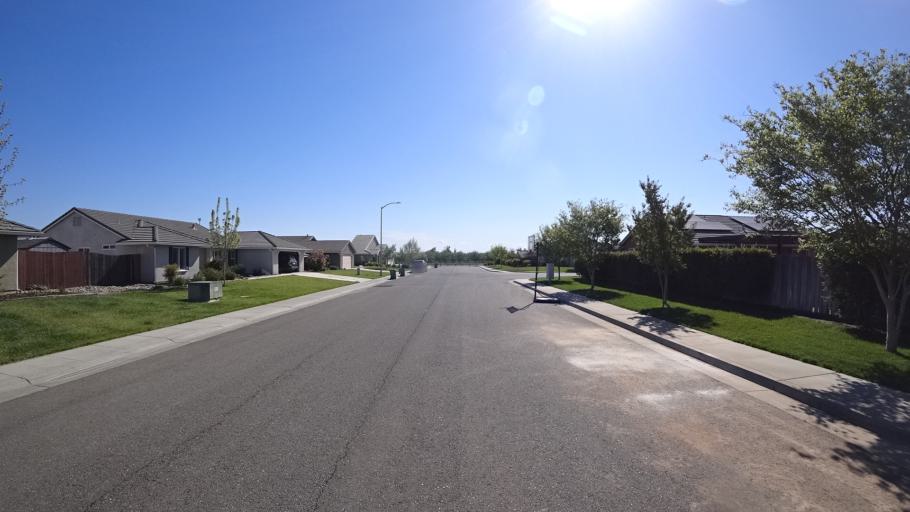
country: US
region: California
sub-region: Glenn County
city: Orland
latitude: 39.7379
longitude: -122.1676
